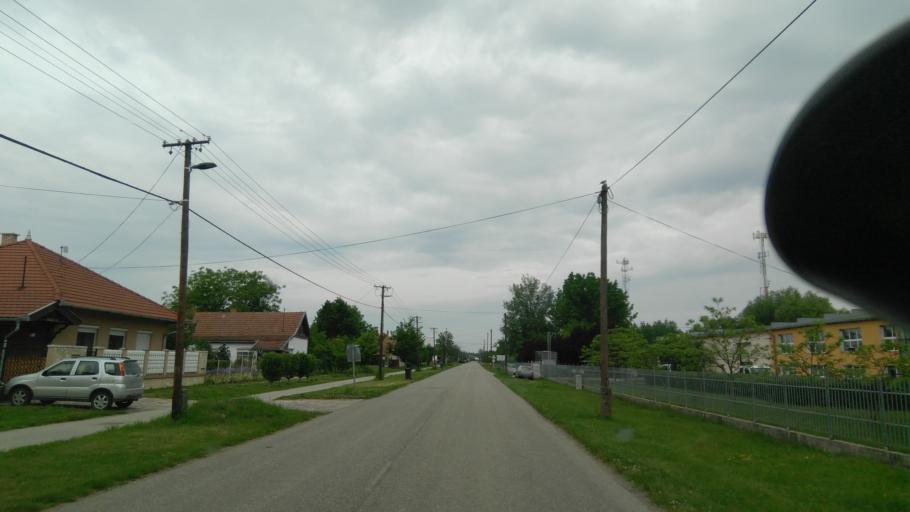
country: HU
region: Bekes
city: Veszto
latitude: 46.9154
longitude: 21.2564
